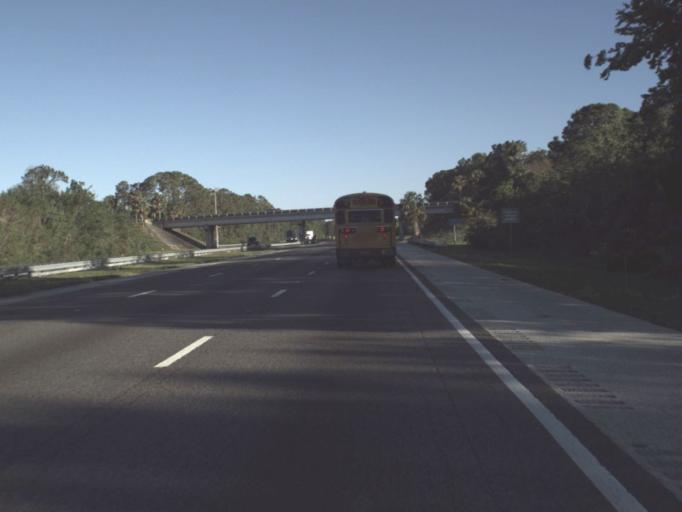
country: US
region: Florida
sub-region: Flagler County
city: Flagler Beach
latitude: 29.4055
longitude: -81.1561
